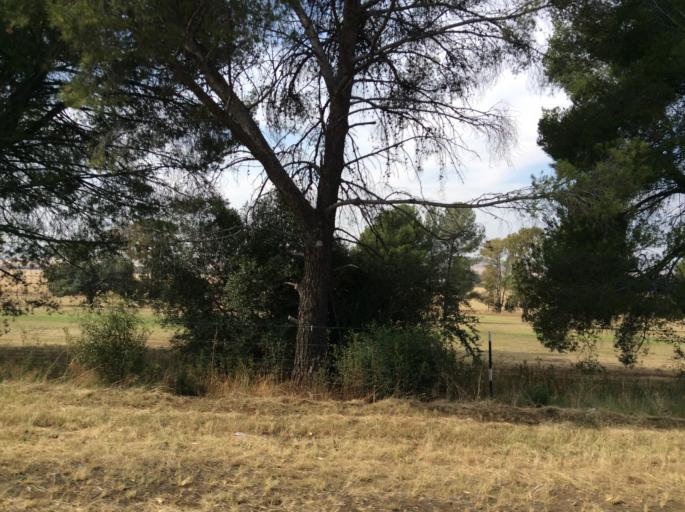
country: ZA
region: Orange Free State
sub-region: Xhariep District Municipality
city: Dewetsdorp
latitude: -29.5702
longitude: 26.6658
